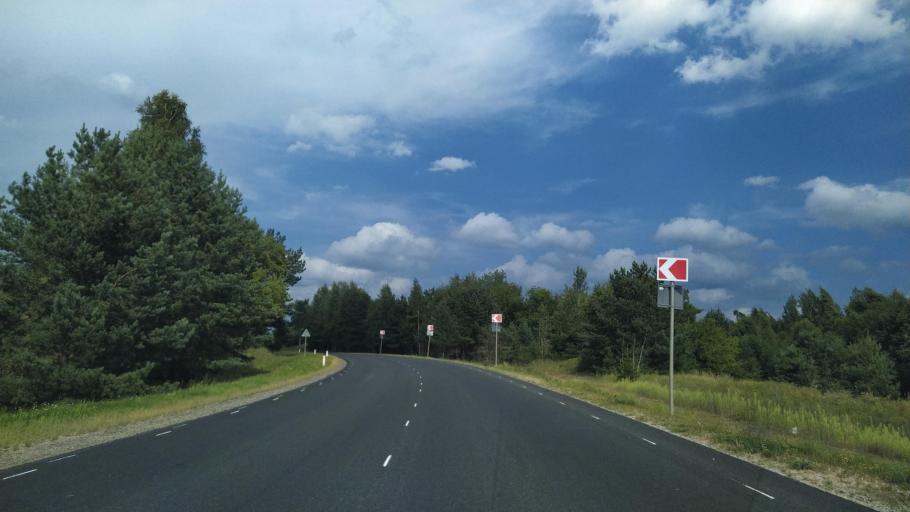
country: RU
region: Pskov
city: Porkhov
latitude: 57.8137
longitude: 29.5066
